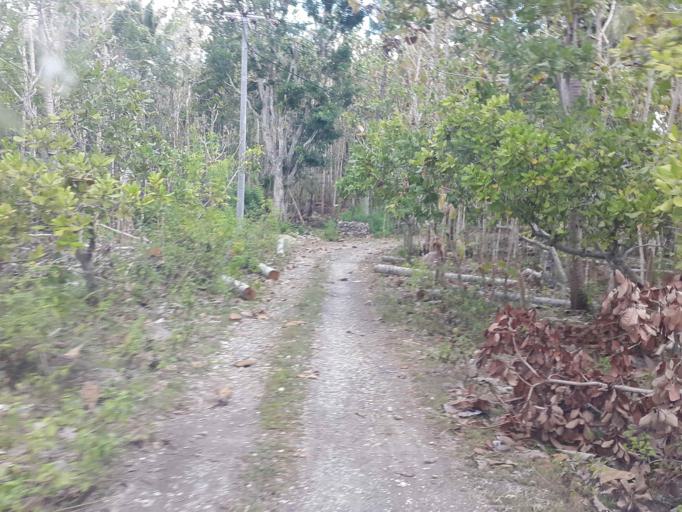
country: ID
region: Bali
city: Klumbu
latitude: -8.7054
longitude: 115.5186
